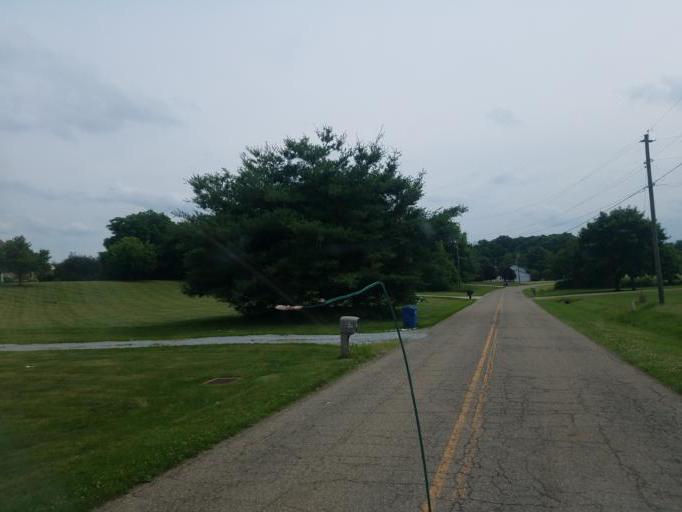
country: US
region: Ohio
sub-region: Knox County
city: Fredericktown
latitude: 40.4822
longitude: -82.5282
